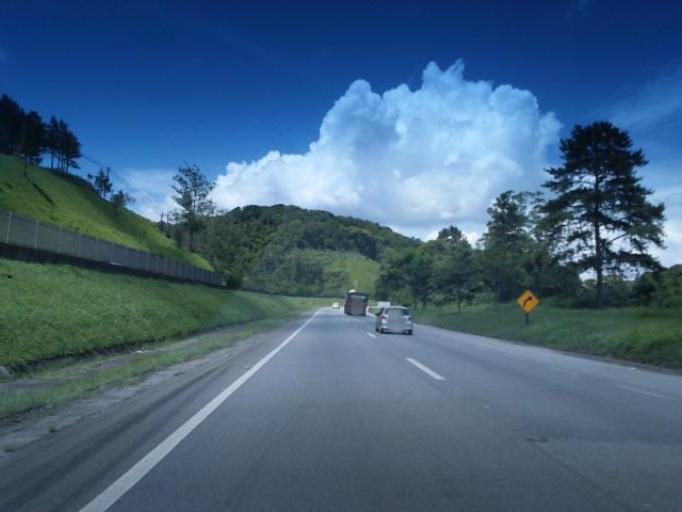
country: BR
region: Sao Paulo
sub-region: Juquitiba
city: Juquitiba
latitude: -23.9392
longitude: -47.0403
